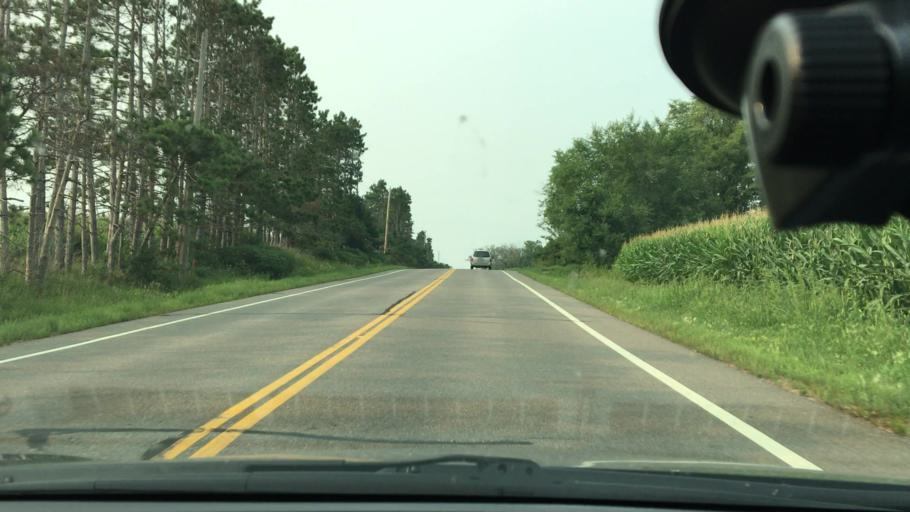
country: US
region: Minnesota
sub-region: Hennepin County
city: Champlin
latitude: 45.1766
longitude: -93.4623
